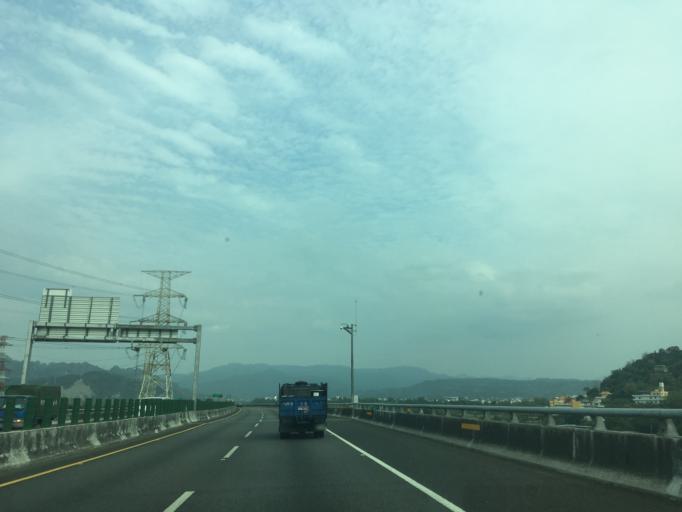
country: TW
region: Taiwan
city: Zhongxing New Village
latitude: 24.0085
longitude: 120.7088
